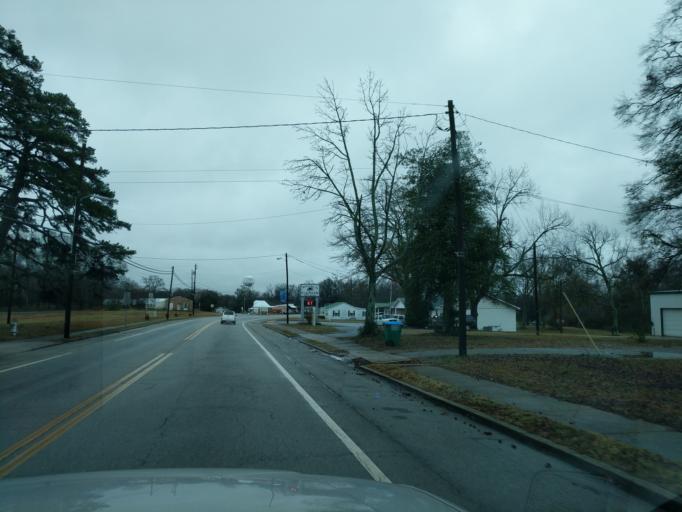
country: US
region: Georgia
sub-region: Hart County
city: Royston
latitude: 34.3450
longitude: -83.1101
